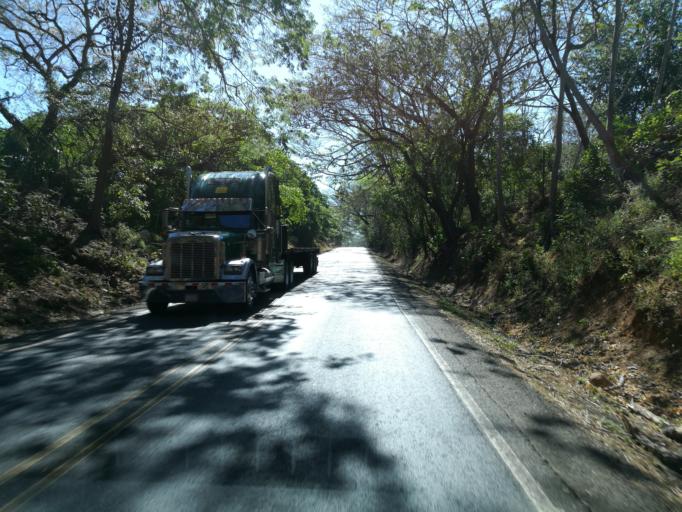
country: CR
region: Puntarenas
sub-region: Canton Central de Puntarenas
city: Puntarenas
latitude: 10.1019
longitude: -84.8725
